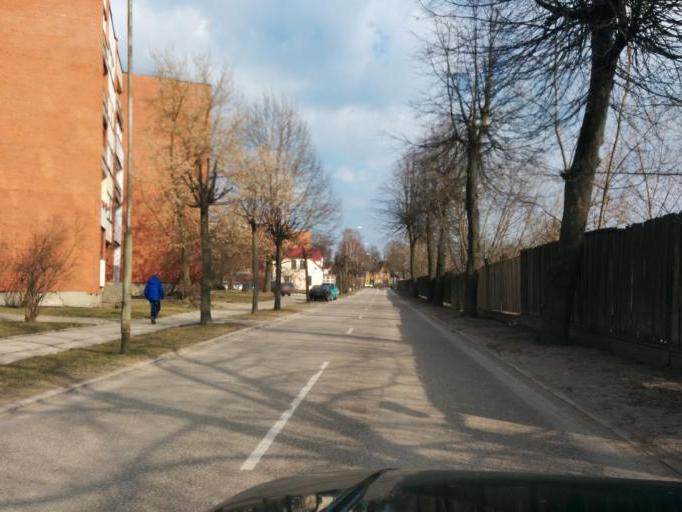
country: LV
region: Jelgava
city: Jelgava
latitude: 56.6488
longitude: 23.7041
